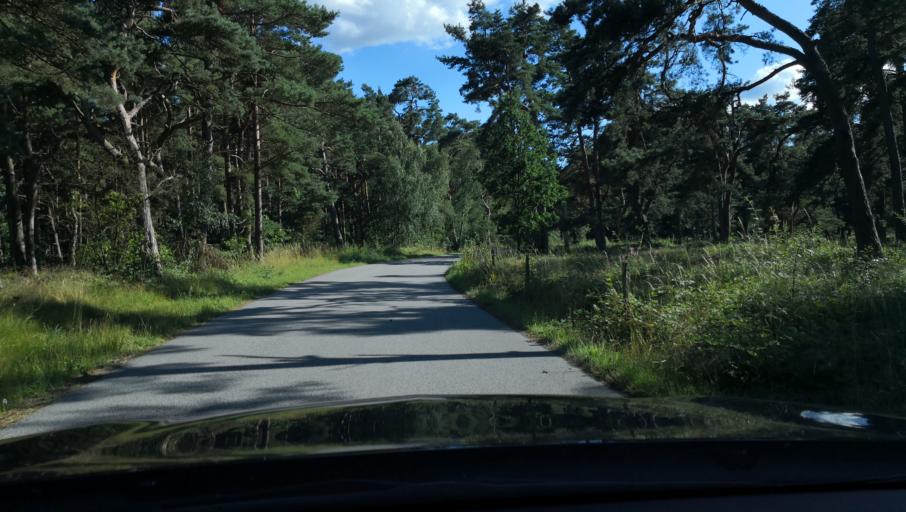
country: SE
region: Skane
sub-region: Simrishamns Kommun
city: Kivik
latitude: 55.7894
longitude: 14.1970
